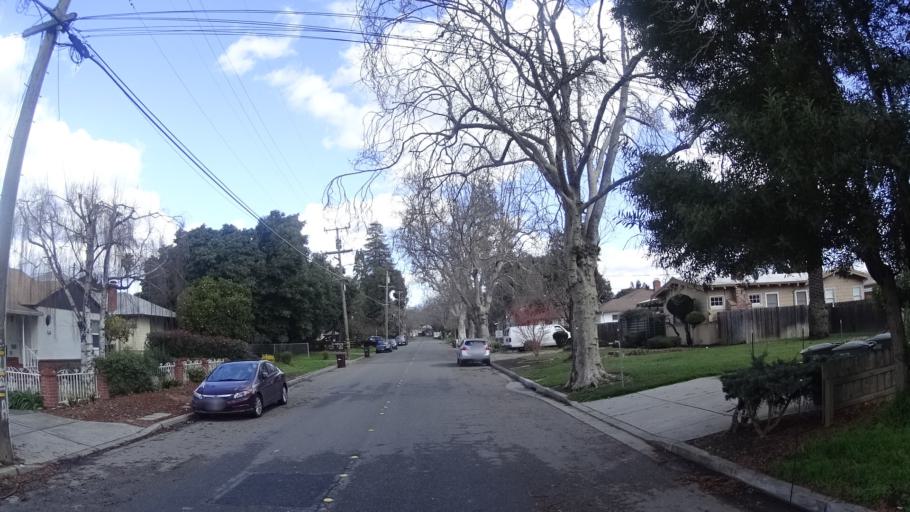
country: US
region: California
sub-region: Alameda County
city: Cherryland
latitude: 37.6813
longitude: -122.1012
